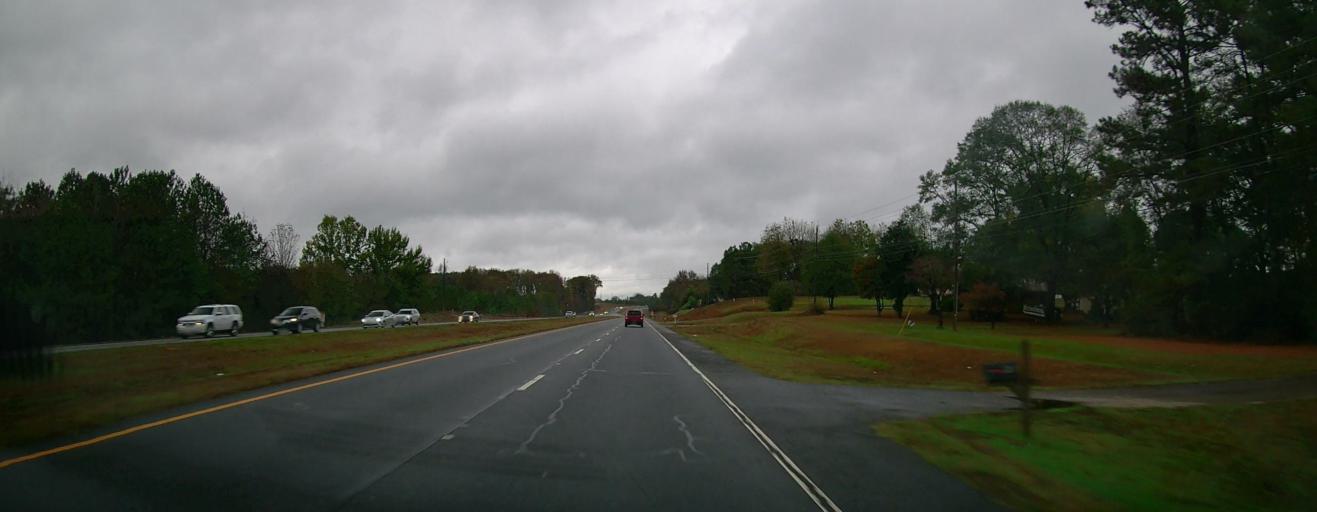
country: US
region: Georgia
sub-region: Jackson County
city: Commerce
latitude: 34.1598
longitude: -83.4439
